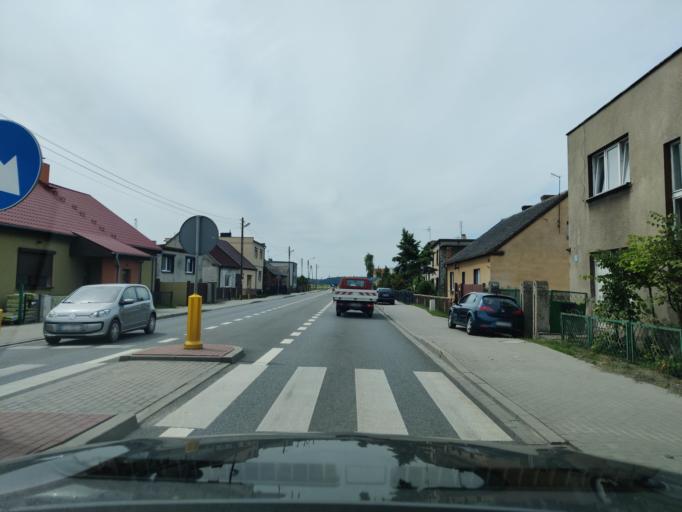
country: PL
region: Greater Poland Voivodeship
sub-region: Powiat grodziski
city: Granowo
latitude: 52.2451
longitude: 16.6114
